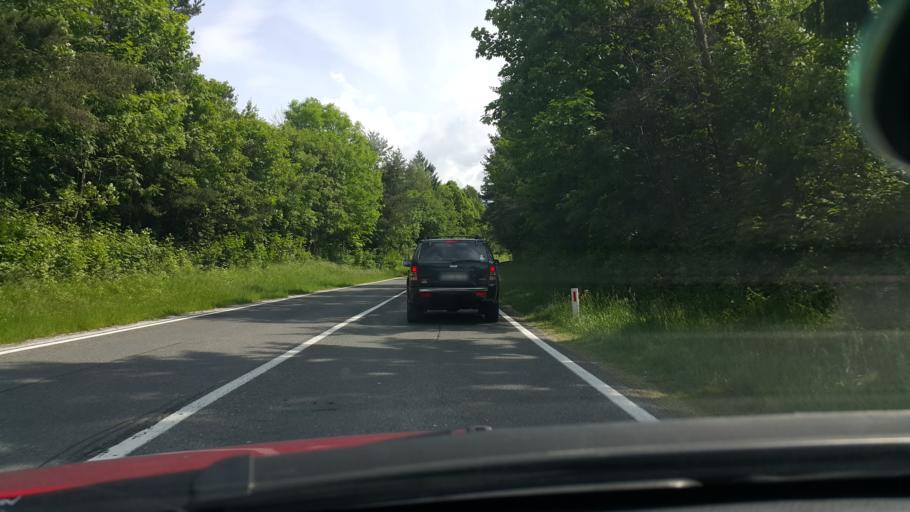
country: SI
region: Trzic
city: Bistrica pri Trzicu
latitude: 46.3481
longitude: 14.2876
